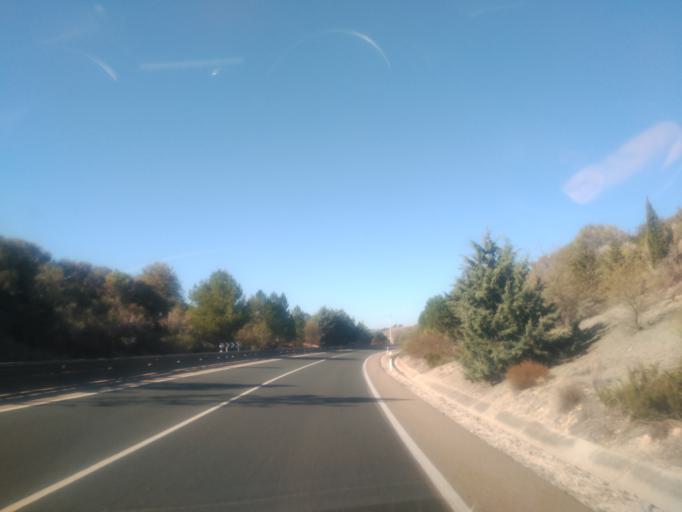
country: ES
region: Castille and Leon
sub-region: Provincia de Valladolid
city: Quintanilla de Onesimo
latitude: 41.6186
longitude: -4.3615
